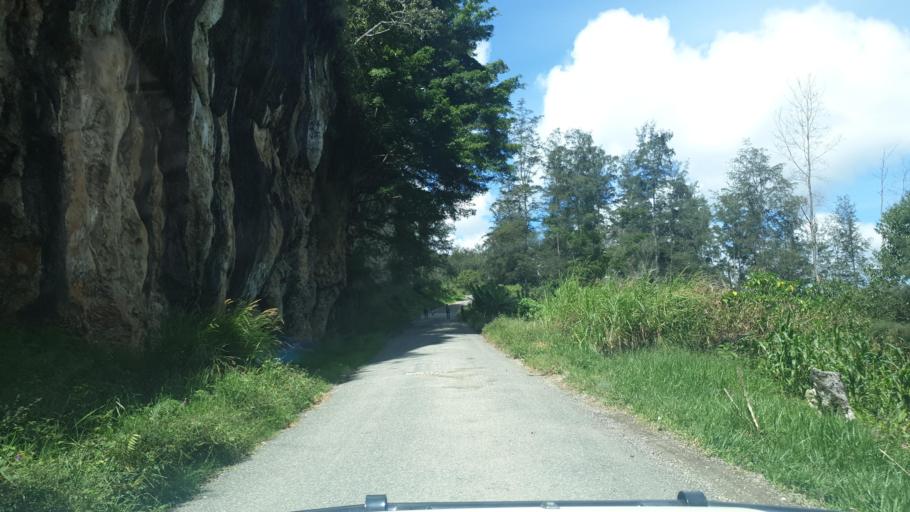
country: PG
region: Chimbu
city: Kundiawa
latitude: -6.1496
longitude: 145.1338
